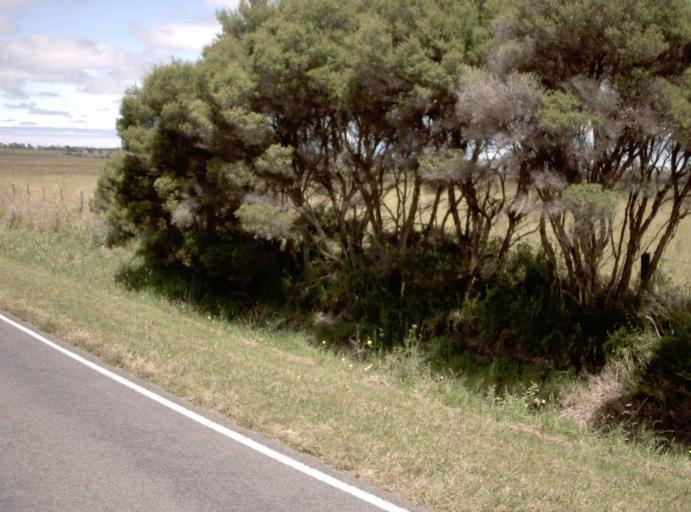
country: AU
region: Victoria
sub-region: Bass Coast
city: North Wonthaggi
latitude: -38.6347
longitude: 146.0121
